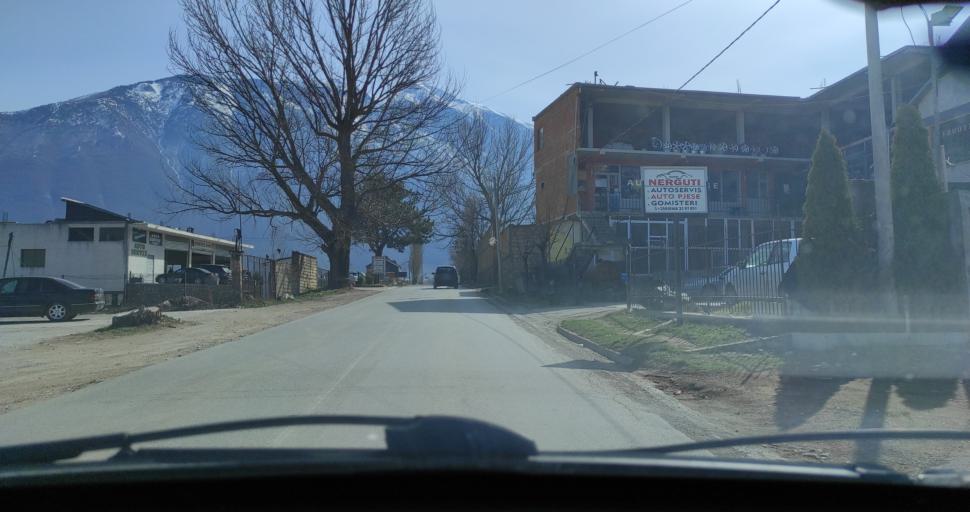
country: AL
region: Kukes
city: Kukes
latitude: 42.0718
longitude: 20.4293
